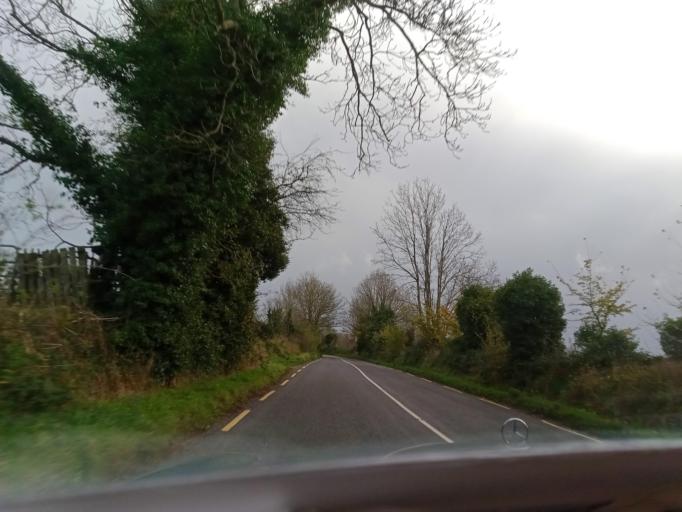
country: IE
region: Leinster
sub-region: Kilkenny
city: Piltown
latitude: 52.3272
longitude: -7.3126
